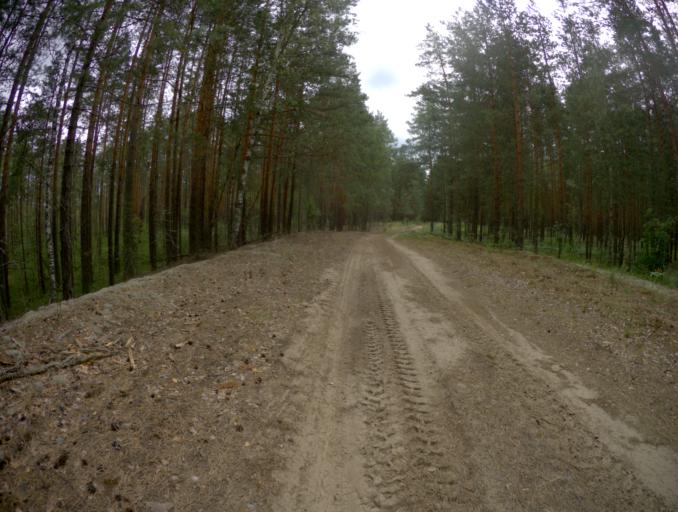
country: RU
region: Nizjnij Novgorod
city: Frolishchi
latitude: 56.3179
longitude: 42.6851
